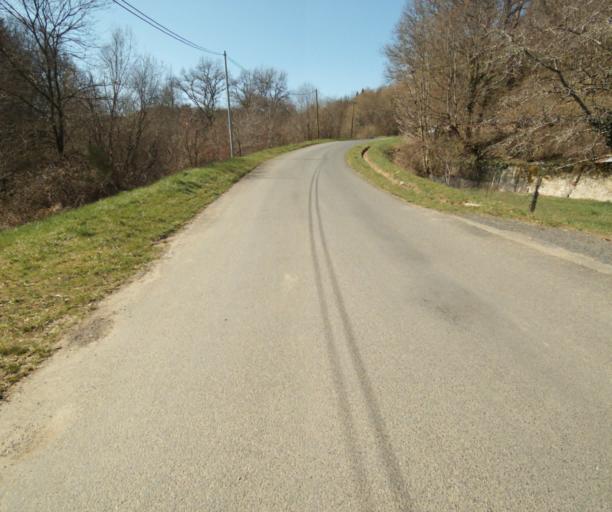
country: FR
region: Limousin
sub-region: Departement de la Correze
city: Naves
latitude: 45.3097
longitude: 1.7243
